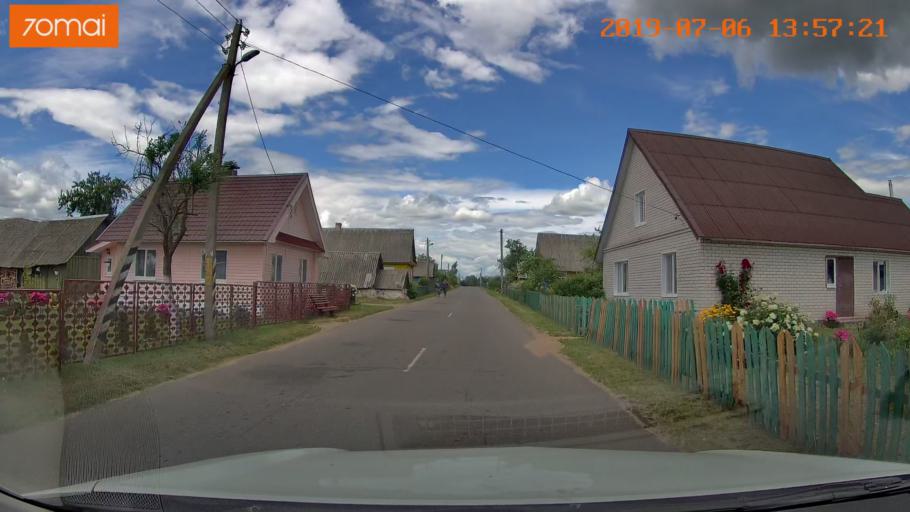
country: BY
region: Minsk
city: Ivyanyets
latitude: 53.7734
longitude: 26.8061
